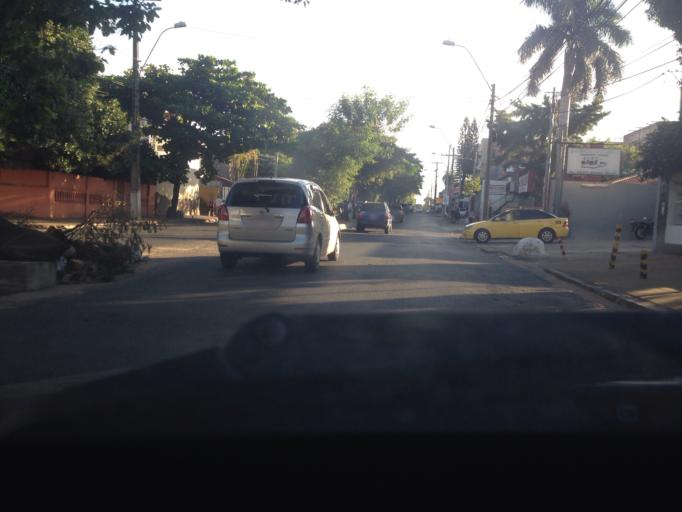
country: PY
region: Central
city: Lambare
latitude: -25.3167
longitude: -57.5906
